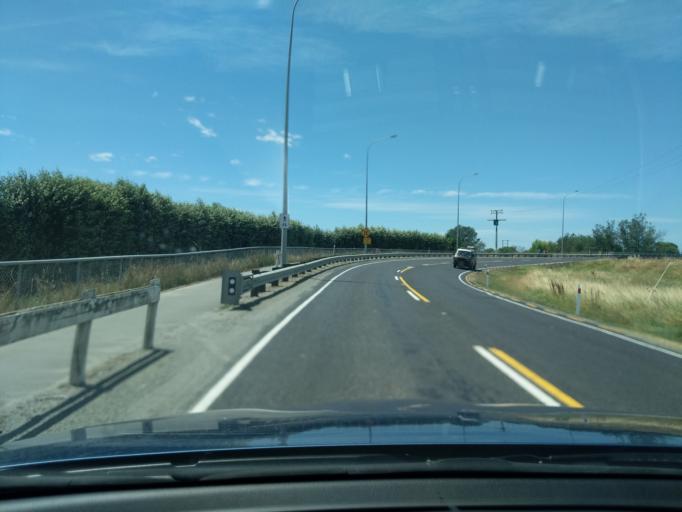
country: NZ
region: Tasman
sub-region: Tasman District
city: Motueka
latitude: -41.0904
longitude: 173.0069
